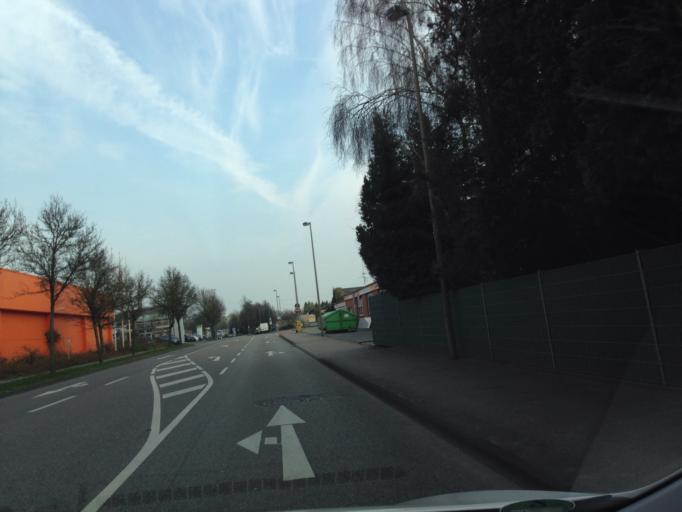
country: DE
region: North Rhine-Westphalia
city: Erkelenz
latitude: 51.0695
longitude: 6.3055
